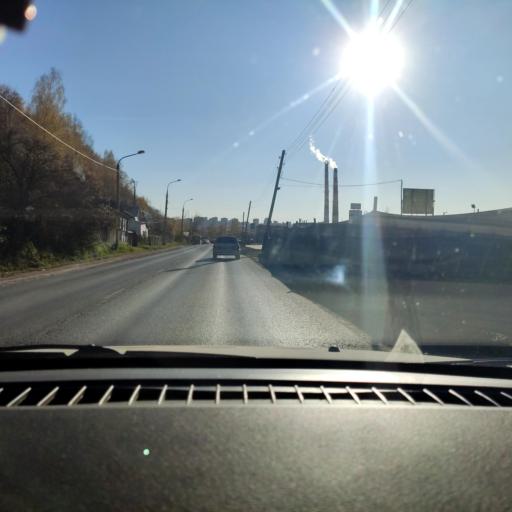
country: RU
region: Perm
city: Perm
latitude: 58.0500
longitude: 56.3260
